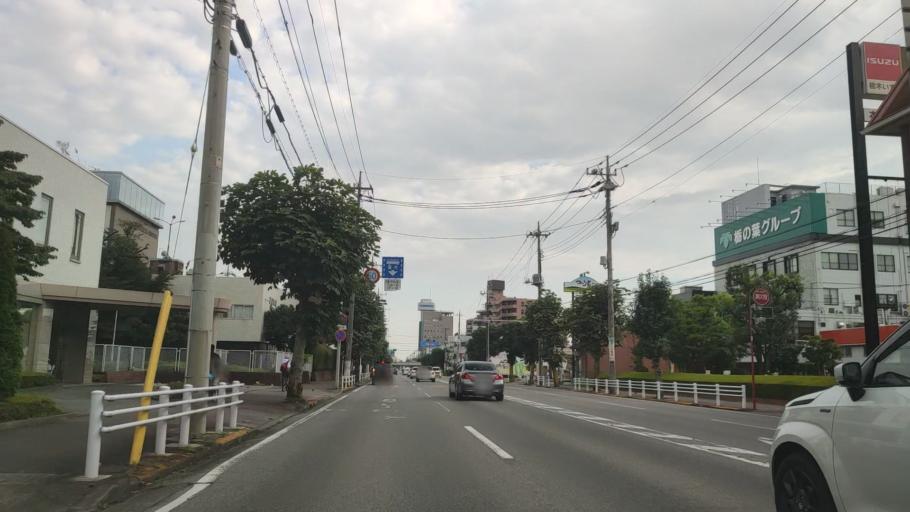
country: JP
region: Tochigi
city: Utsunomiya-shi
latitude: 36.5503
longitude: 139.8798
